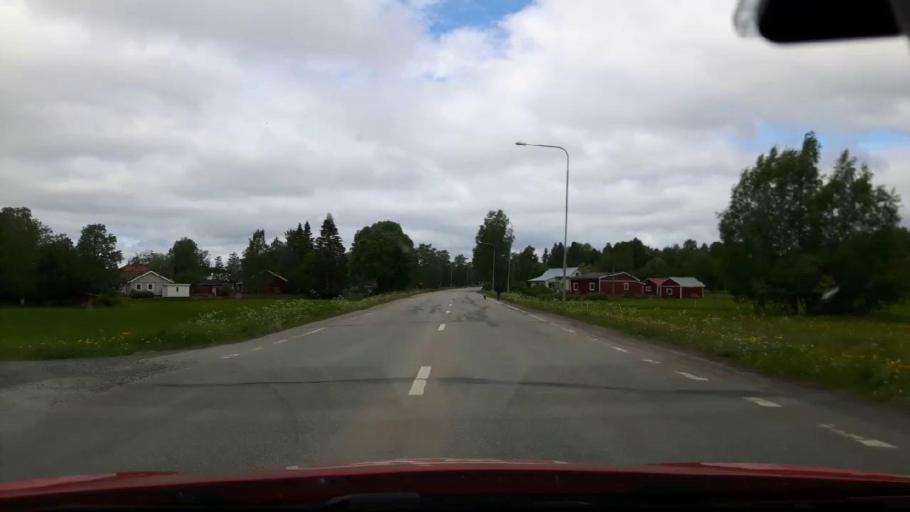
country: SE
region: Jaemtland
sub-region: Krokoms Kommun
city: Krokom
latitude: 63.3087
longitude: 14.4633
